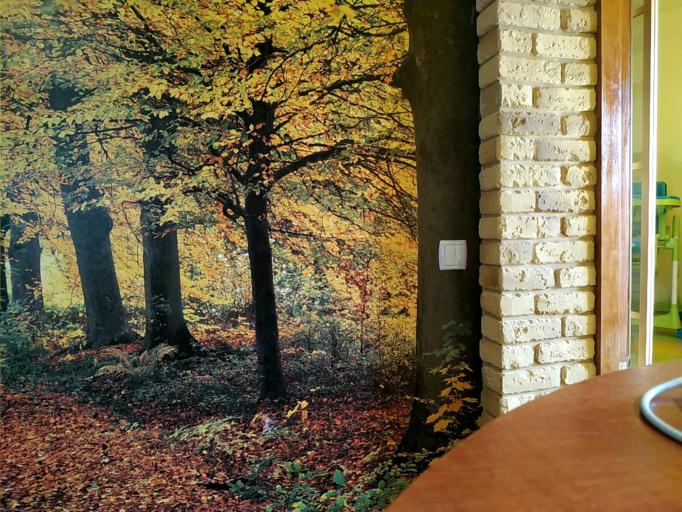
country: RU
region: Tverskaya
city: Kalashnikovo
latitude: 57.3351
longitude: 35.3235
